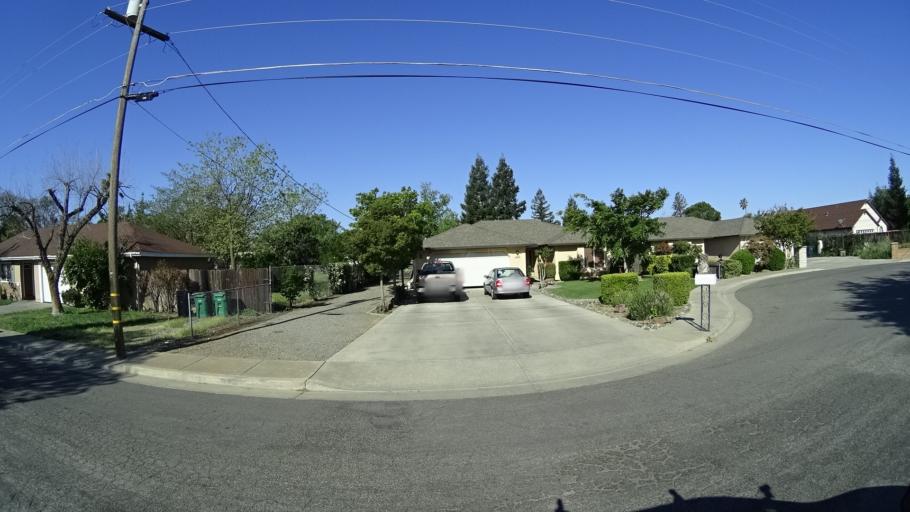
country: US
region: California
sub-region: Glenn County
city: Orland
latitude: 39.7522
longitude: -122.1834
